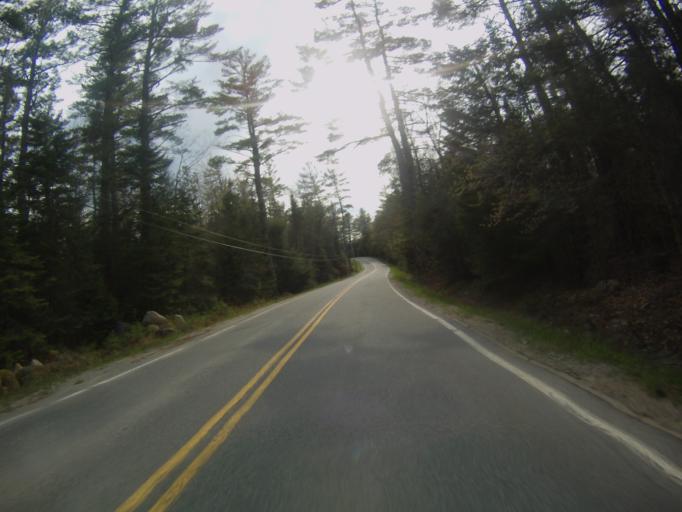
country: US
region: New York
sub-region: Warren County
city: Warrensburg
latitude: 43.8362
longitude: -73.8833
